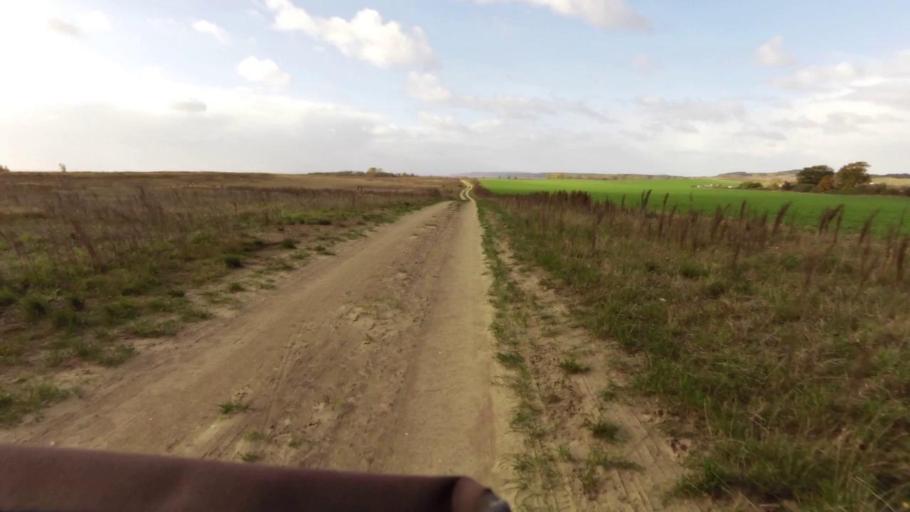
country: PL
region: West Pomeranian Voivodeship
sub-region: Powiat kamienski
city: Wolin
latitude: 53.8401
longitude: 14.6042
